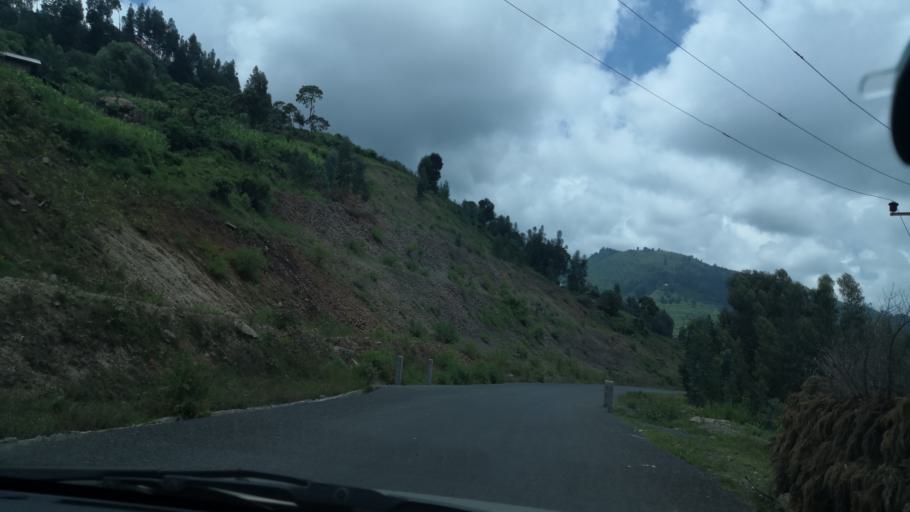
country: ET
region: Amhara
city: Abomsa
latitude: 10.3222
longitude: 39.8529
